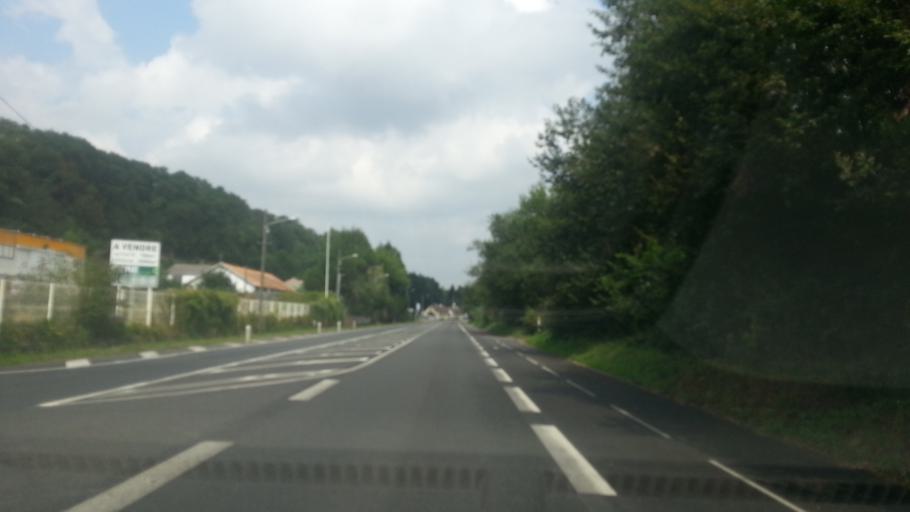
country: FR
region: Picardie
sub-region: Departement de l'Oise
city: Thiverny
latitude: 49.2344
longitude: 2.4360
